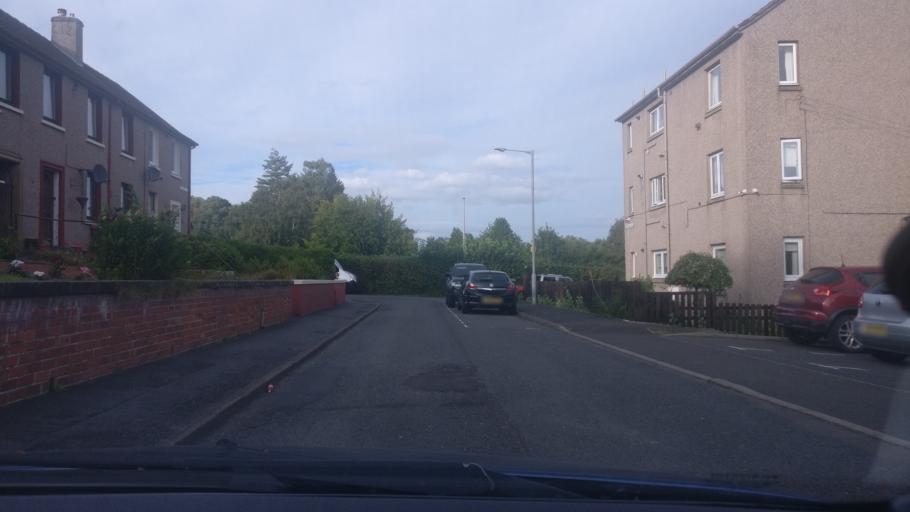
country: GB
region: Scotland
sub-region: The Scottish Borders
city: Hawick
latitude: 55.4347
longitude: -2.7846
